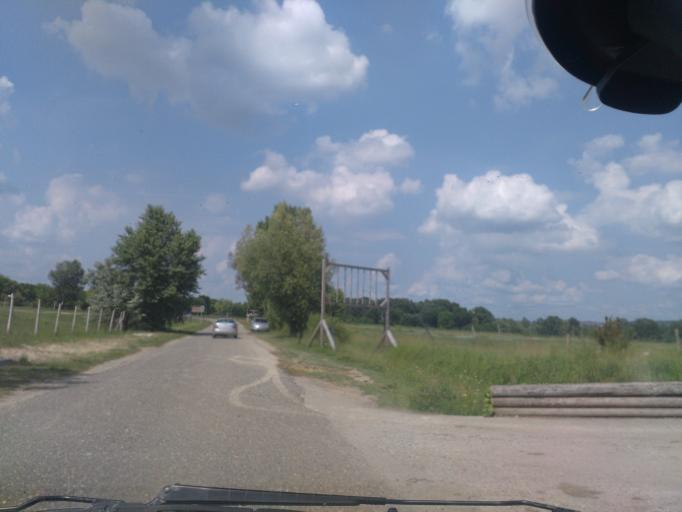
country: HU
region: Pest
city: Veresegyhaz
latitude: 47.6362
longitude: 19.2604
